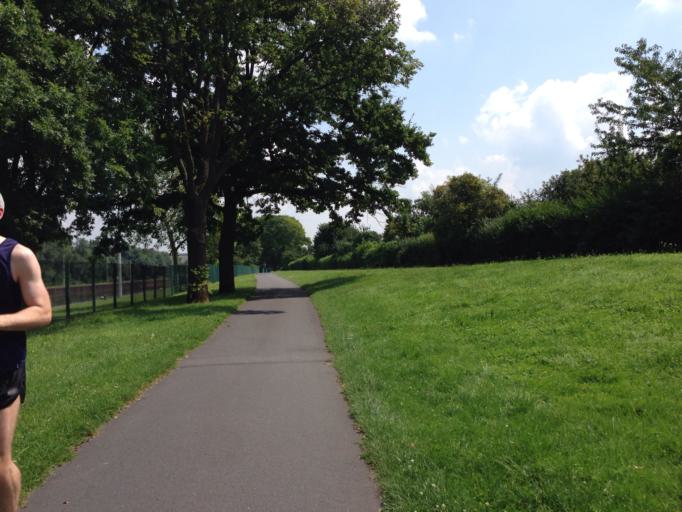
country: DE
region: Hesse
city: Niederrad
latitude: 50.0878
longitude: 8.5902
